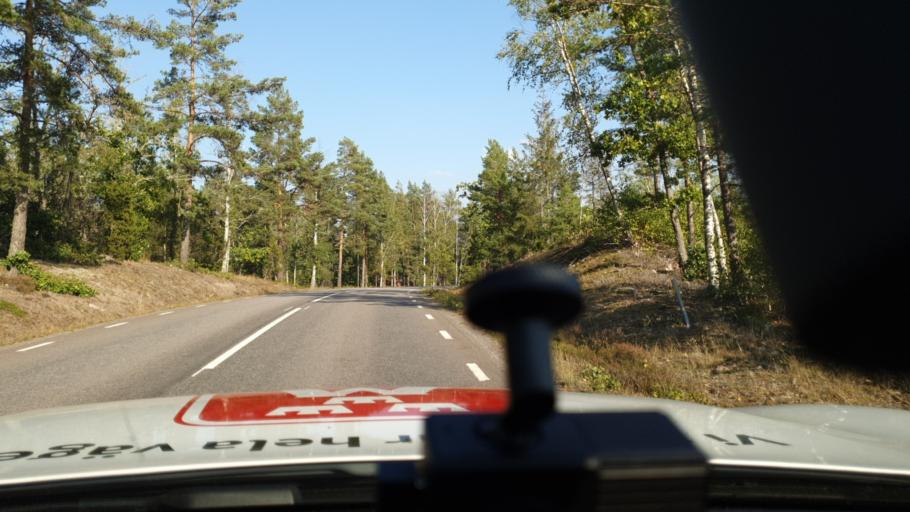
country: SE
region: Kalmar
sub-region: Oskarshamns Kommun
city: Oskarshamn
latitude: 57.4408
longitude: 16.4040
